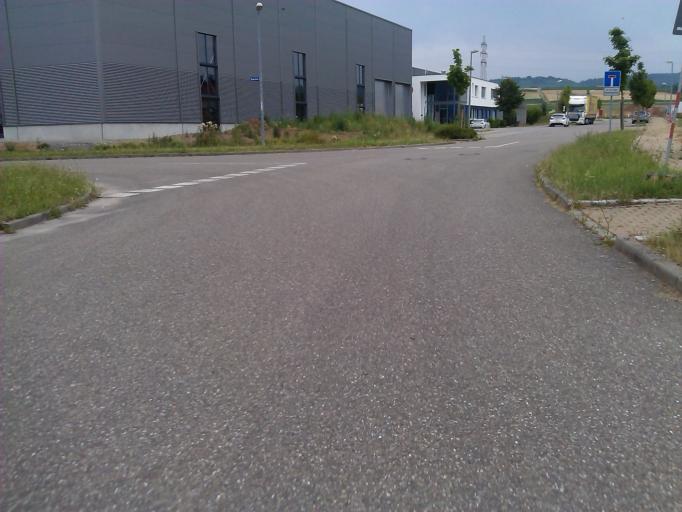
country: DE
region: Baden-Wuerttemberg
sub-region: Regierungsbezirk Stuttgart
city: Cleebronn
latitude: 49.0653
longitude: 9.0387
